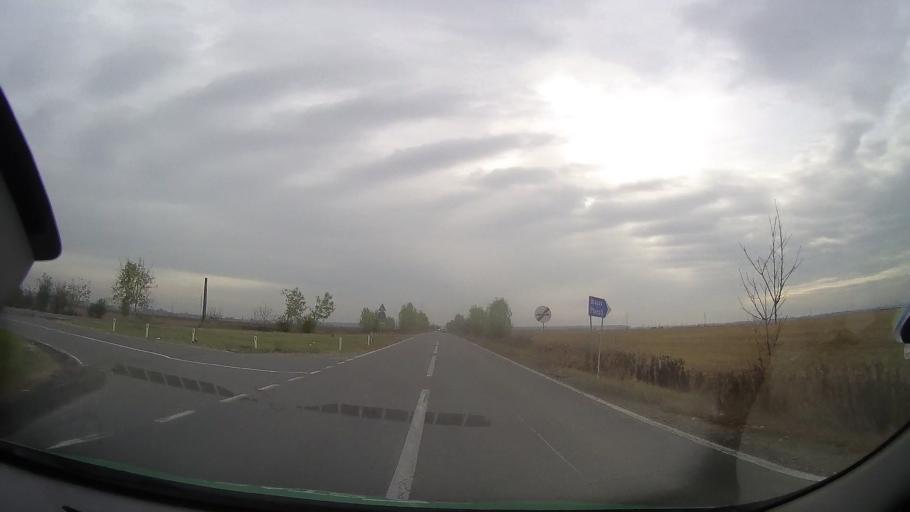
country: RO
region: Prahova
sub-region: Comuna Berceni
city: Berceni
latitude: 44.9378
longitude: 26.1026
